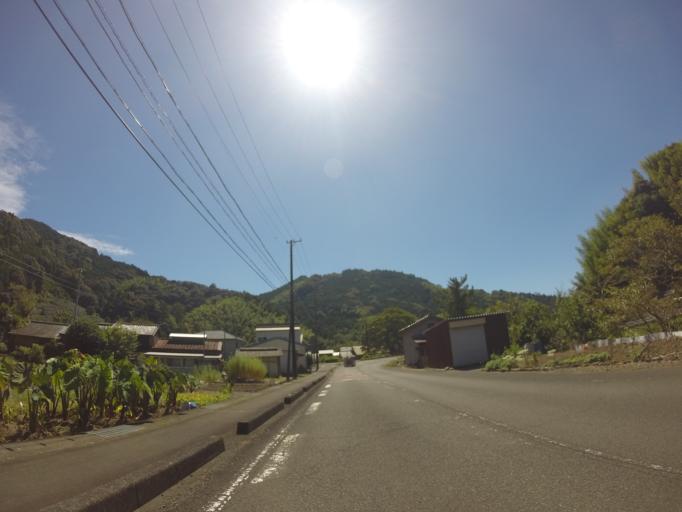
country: JP
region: Shizuoka
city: Fujieda
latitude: 34.9406
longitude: 138.2103
